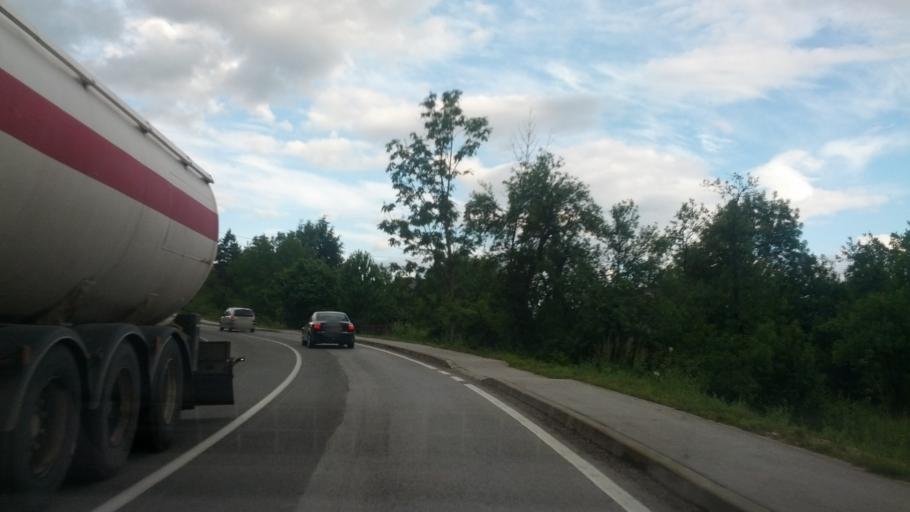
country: HR
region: Licko-Senjska
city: Jezerce
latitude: 44.9583
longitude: 15.6592
